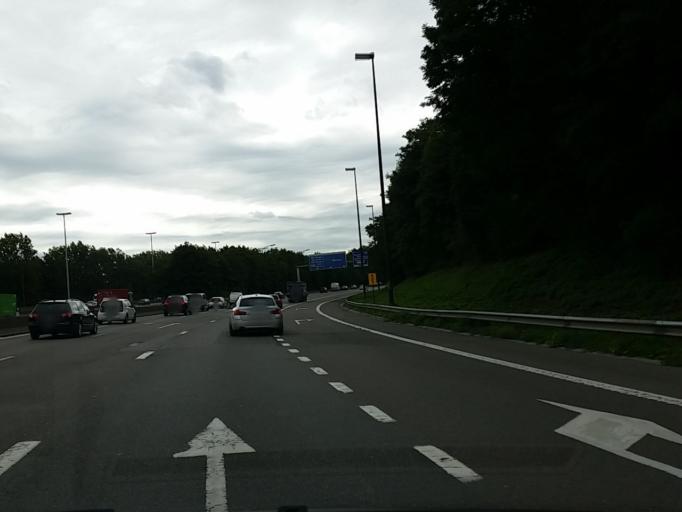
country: BE
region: Flanders
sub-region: Provincie Vlaams-Brabant
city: Zaventem
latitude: 50.8859
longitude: 4.4588
